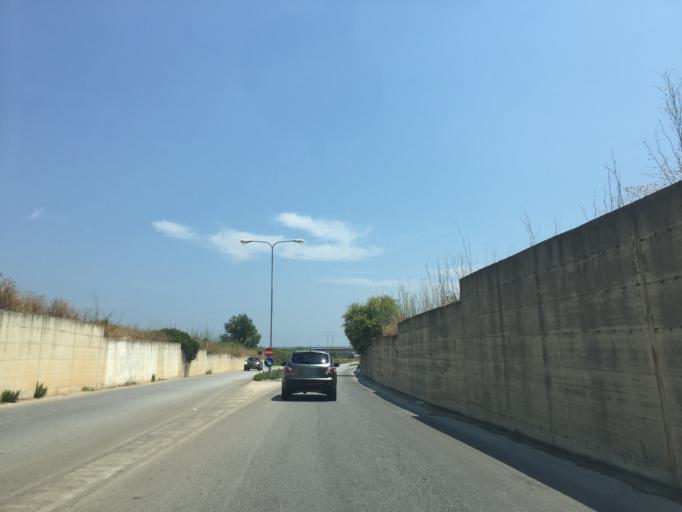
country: IT
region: Sicily
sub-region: Provincia di Siracusa
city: Avola
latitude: 36.9210
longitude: 15.1395
